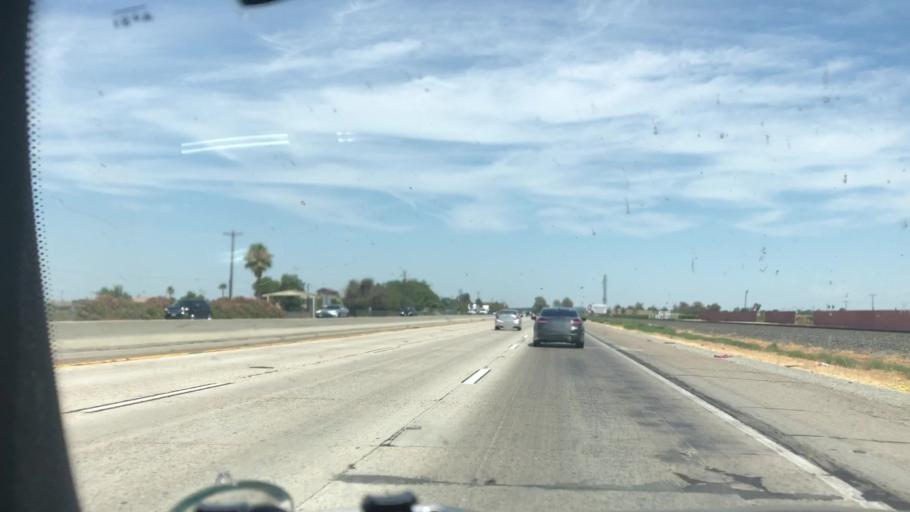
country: US
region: California
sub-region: Kern County
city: McFarland
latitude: 35.6644
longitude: -119.2238
